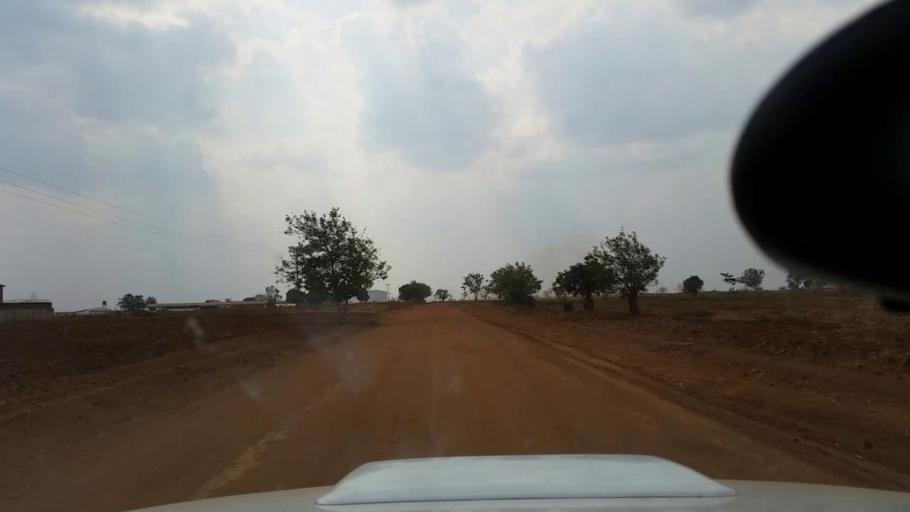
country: MW
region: Central Region
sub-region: Lilongwe District
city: Lilongwe
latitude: -13.7949
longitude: 33.7724
